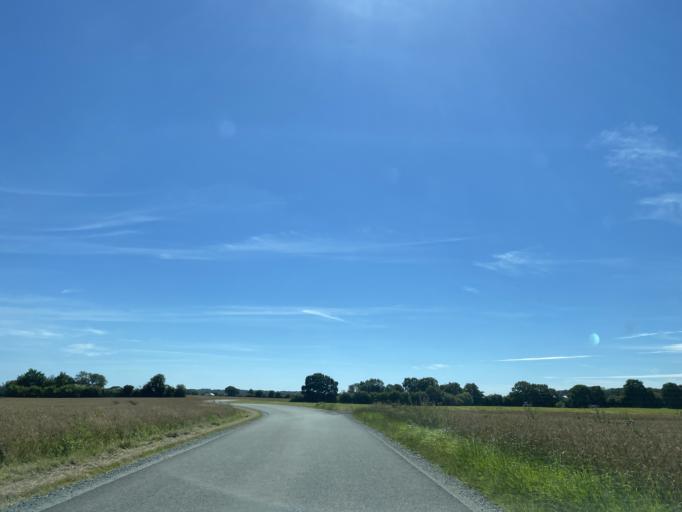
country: DK
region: South Denmark
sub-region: Vejle Kommune
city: Vejle
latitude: 55.6125
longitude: 9.5341
